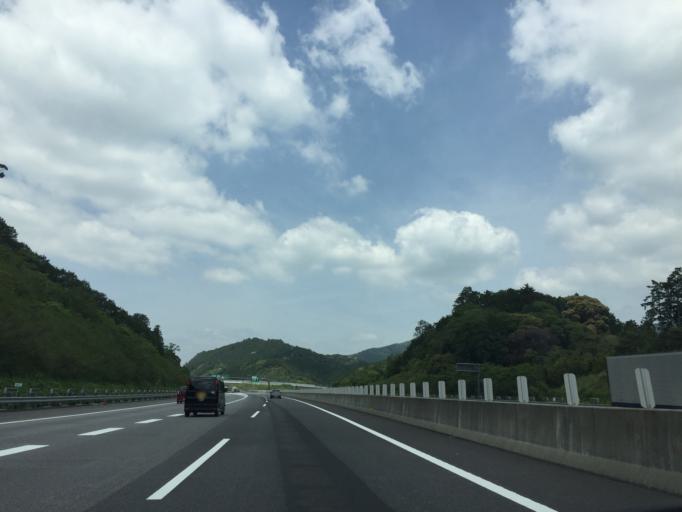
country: JP
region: Shizuoka
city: Hamakita
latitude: 34.8859
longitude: 137.6549
